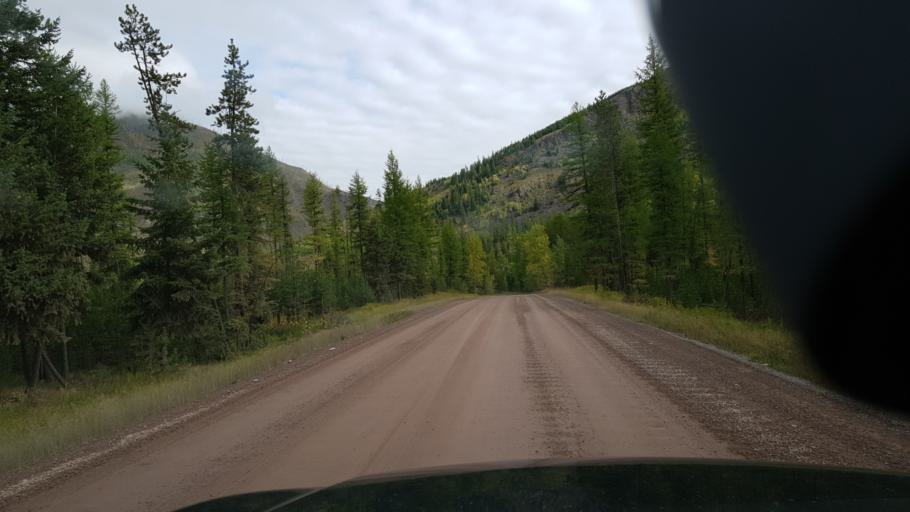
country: US
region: Montana
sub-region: Flathead County
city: Columbia Falls
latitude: 48.5984
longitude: -114.1665
